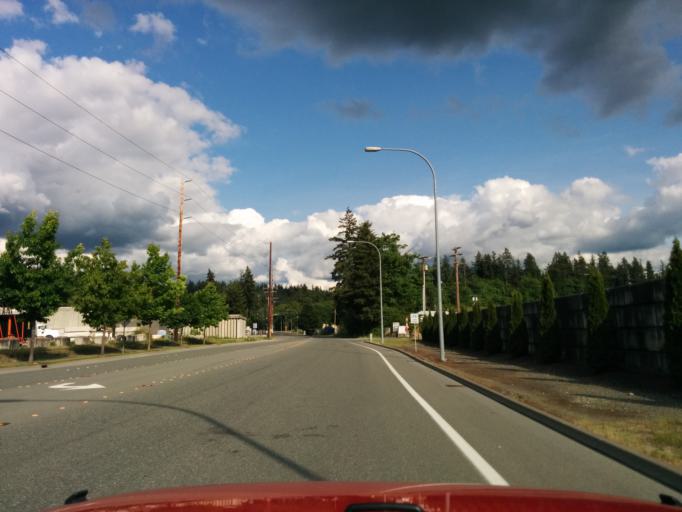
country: US
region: Washington
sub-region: King County
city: Redmond
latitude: 47.6762
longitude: -122.0876
